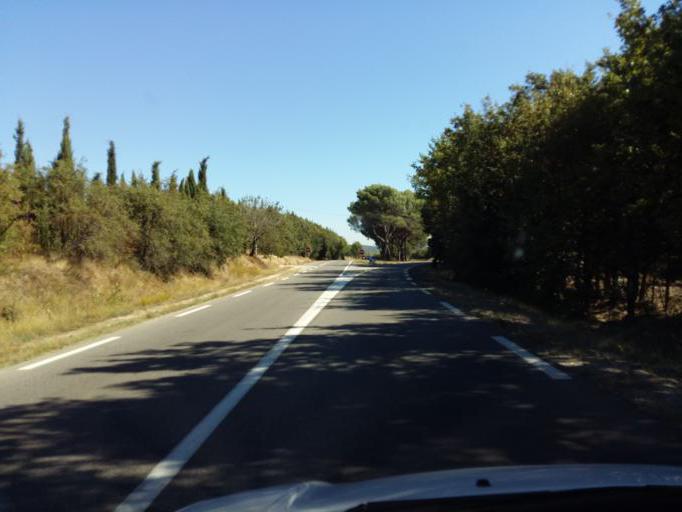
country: FR
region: Provence-Alpes-Cote d'Azur
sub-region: Departement du Vaucluse
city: Merindol
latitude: 43.7527
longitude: 5.2191
